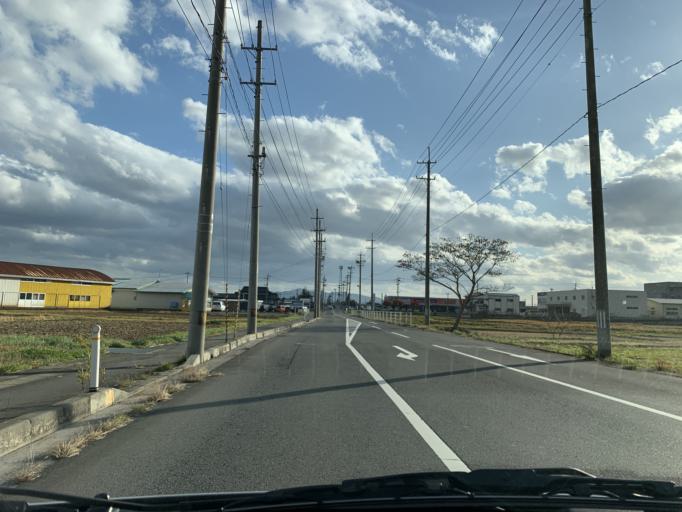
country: JP
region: Iwate
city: Mizusawa
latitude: 39.1550
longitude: 141.1583
